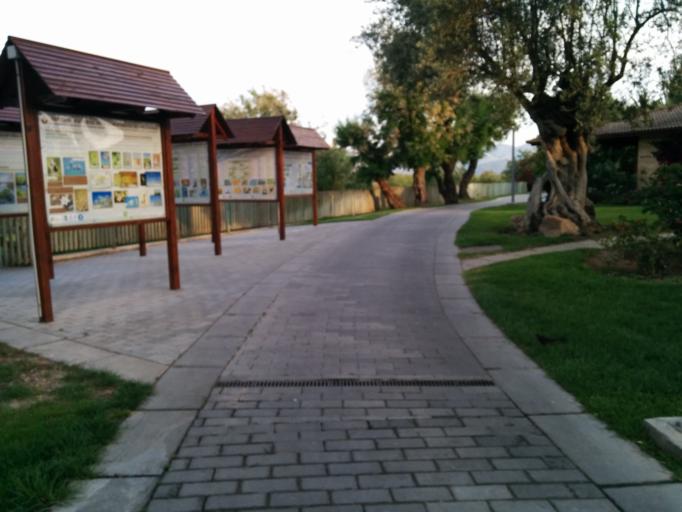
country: ES
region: Balearic Islands
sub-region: Illes Balears
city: Alcudia
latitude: 39.8631
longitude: 3.0922
